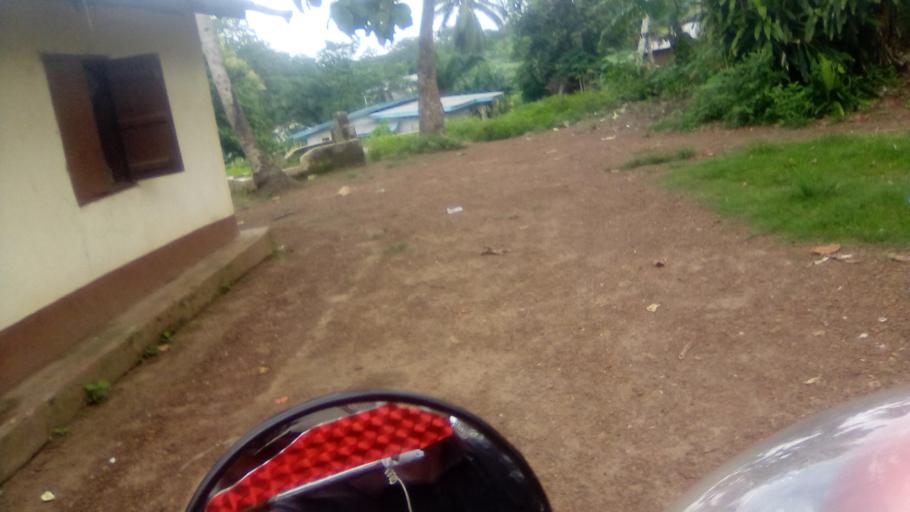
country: SL
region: Southern Province
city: Moyamba
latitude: 8.1556
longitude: -12.4279
